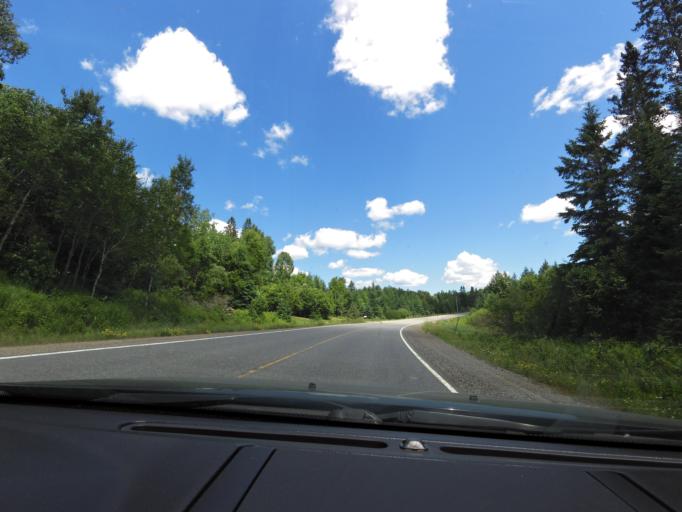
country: CA
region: Ontario
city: Huntsville
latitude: 45.5345
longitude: -79.2935
